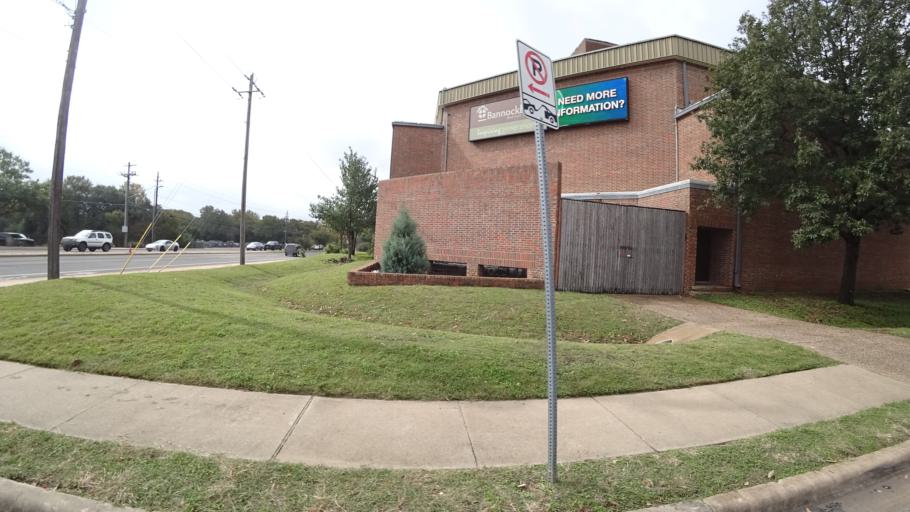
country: US
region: Texas
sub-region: Travis County
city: Shady Hollow
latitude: 30.2129
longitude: -97.8313
